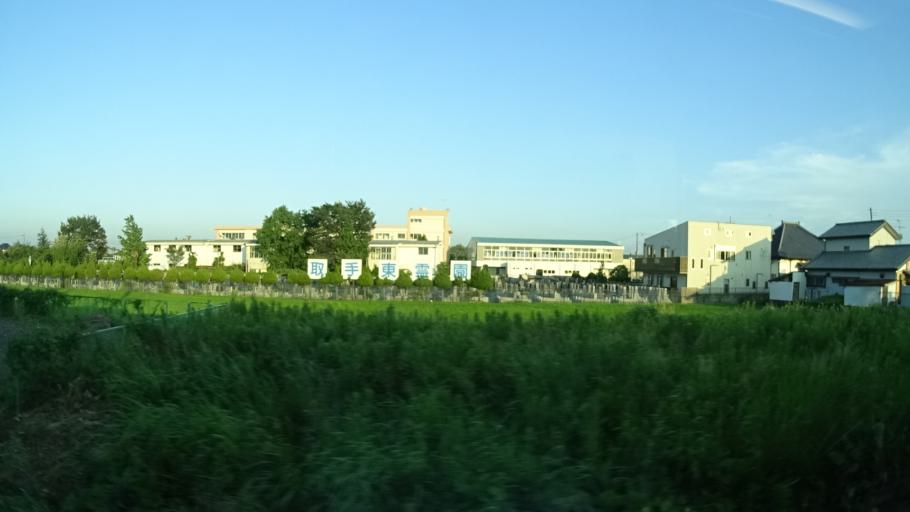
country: JP
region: Ibaraki
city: Toride
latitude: 35.9135
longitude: 140.0925
